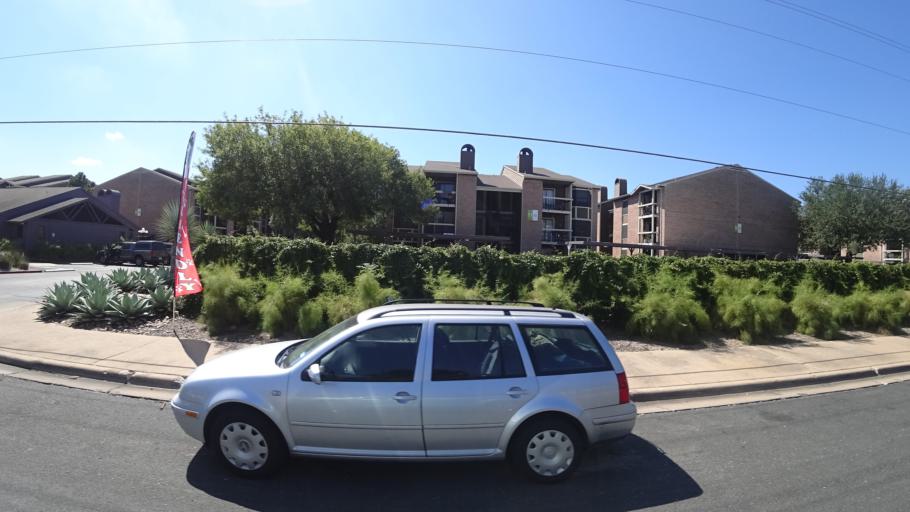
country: US
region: Texas
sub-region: Travis County
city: Austin
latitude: 30.3192
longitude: -97.7038
